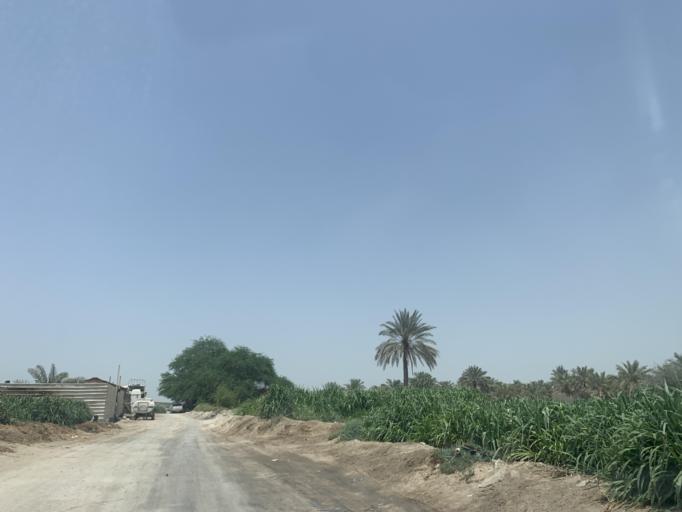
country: BH
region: Central Governorate
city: Madinat Hamad
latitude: 26.1547
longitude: 50.4986
